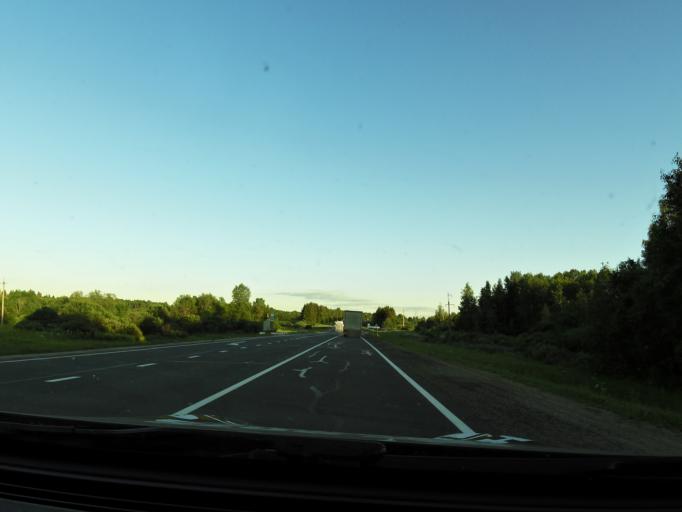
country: RU
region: Vologda
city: Gryazovets
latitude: 58.7295
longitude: 40.2937
